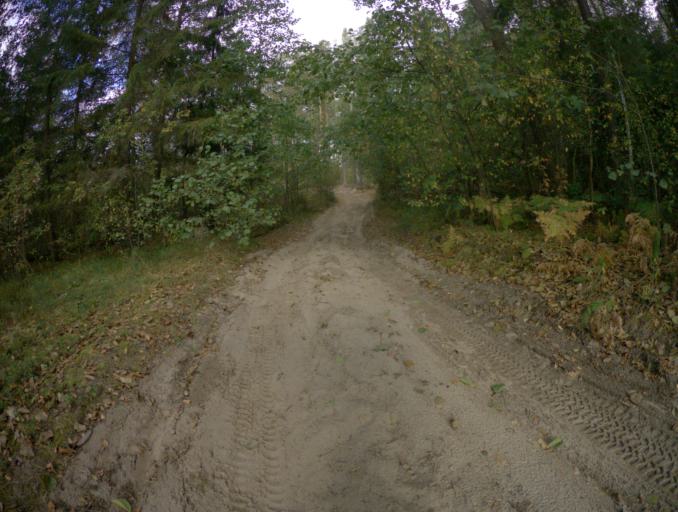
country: RU
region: Moskovskaya
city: Baksheyevo
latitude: 55.7339
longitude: 39.8332
